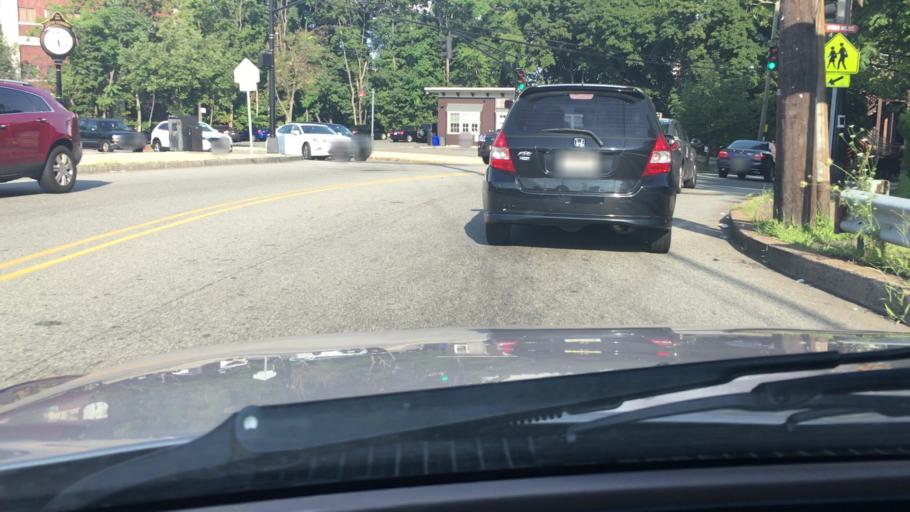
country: US
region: New Jersey
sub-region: Passaic County
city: Paterson
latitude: 40.9147
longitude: -74.1805
